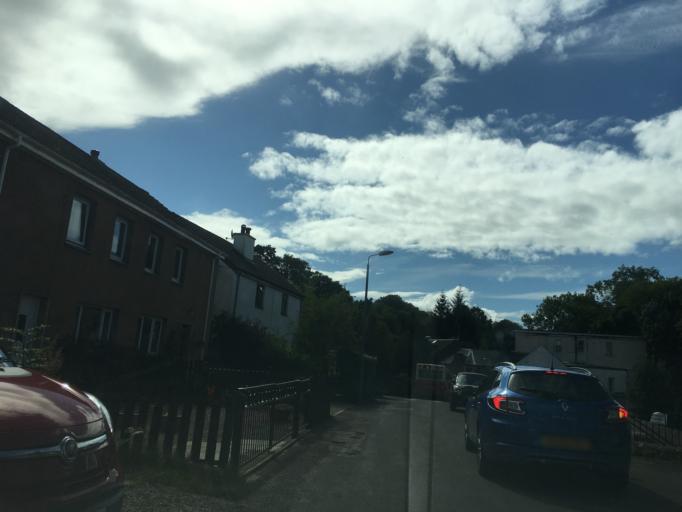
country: GB
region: Scotland
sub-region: Argyll and Bute
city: Oban
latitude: 56.4530
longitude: -5.3843
